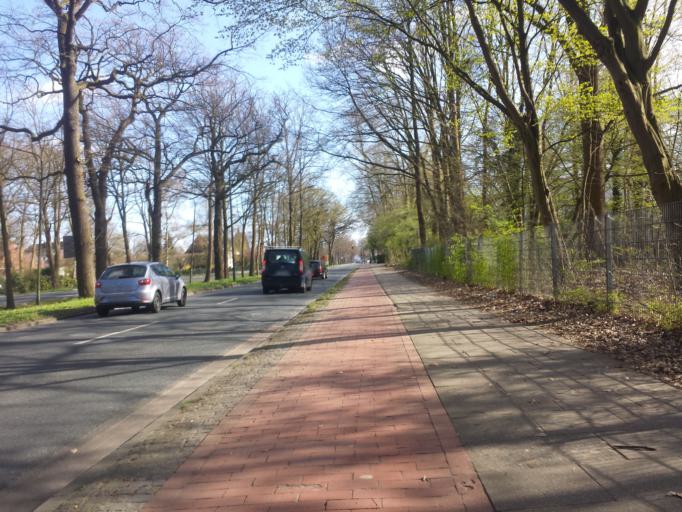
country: DE
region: Lower Saxony
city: Lilienthal
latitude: 53.0783
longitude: 8.8790
